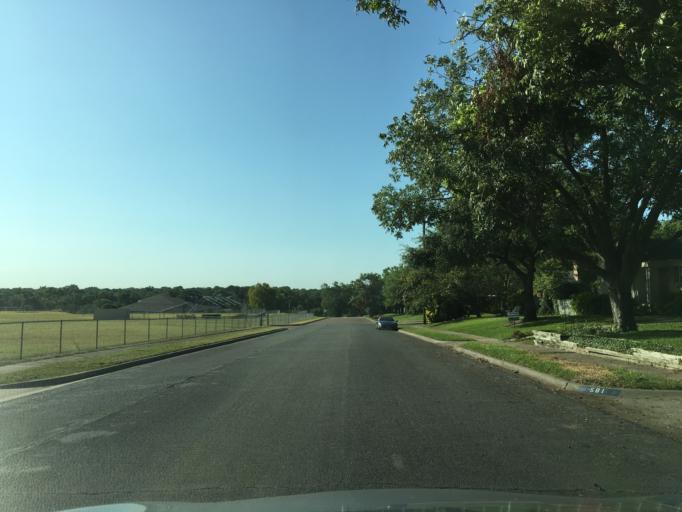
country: US
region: Texas
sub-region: Dallas County
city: Garland
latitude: 32.8549
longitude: -96.7055
